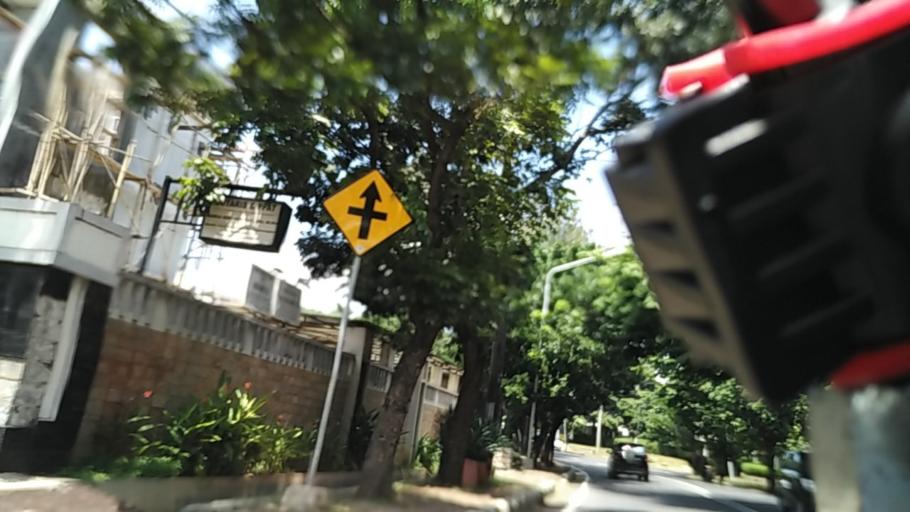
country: ID
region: Central Java
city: Semarang
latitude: -7.0061
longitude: 110.4142
